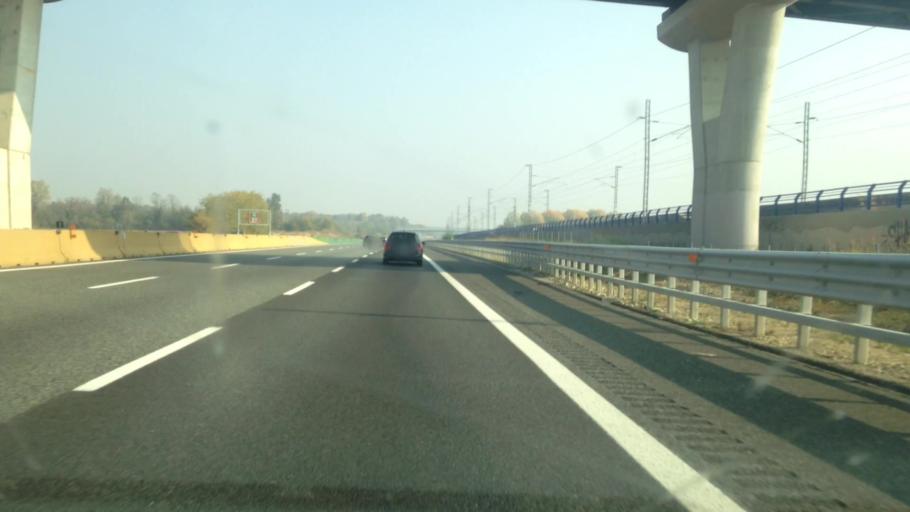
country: IT
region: Piedmont
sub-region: Provincia di Vercelli
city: Carisio
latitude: 45.4067
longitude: 8.1656
